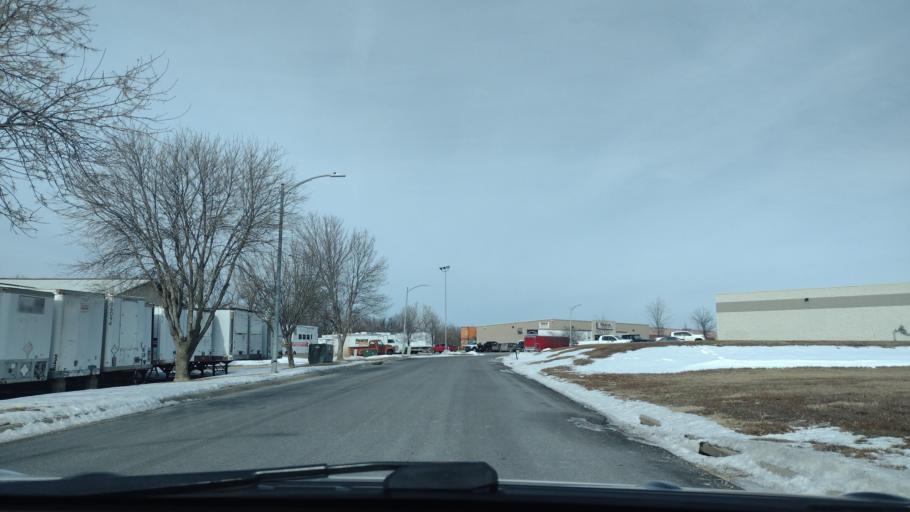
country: US
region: Nebraska
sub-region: Sarpy County
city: Papillion
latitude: 41.1399
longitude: -96.0272
